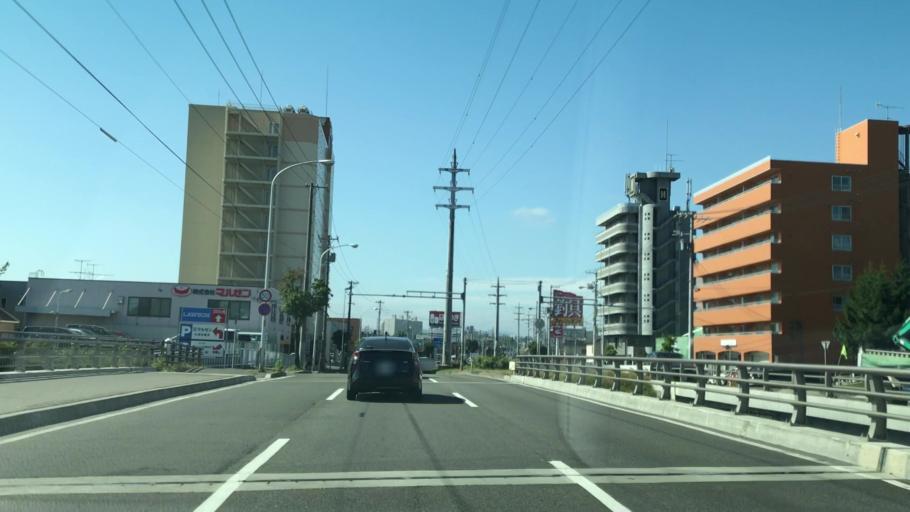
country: JP
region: Hokkaido
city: Sapporo
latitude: 43.0661
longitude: 141.4085
